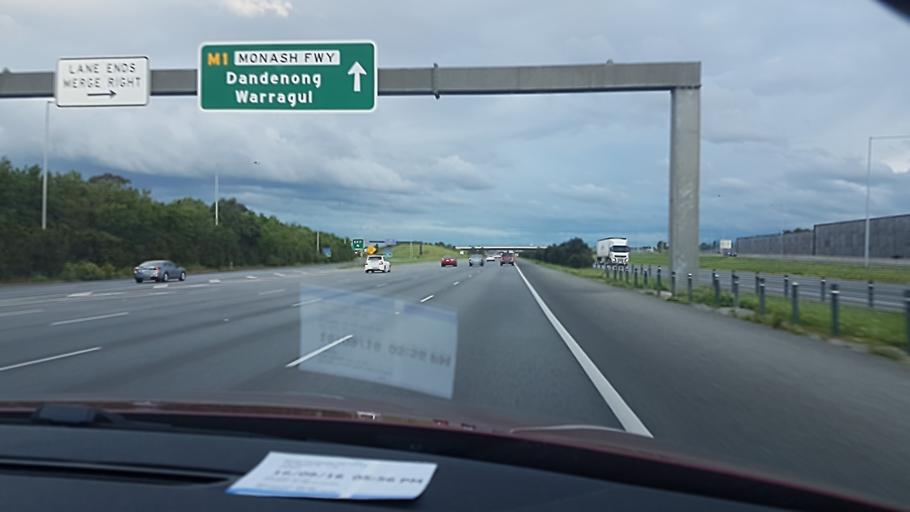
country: AU
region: Victoria
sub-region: Greater Dandenong
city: Noble Park North
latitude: -37.9408
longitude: 145.1994
